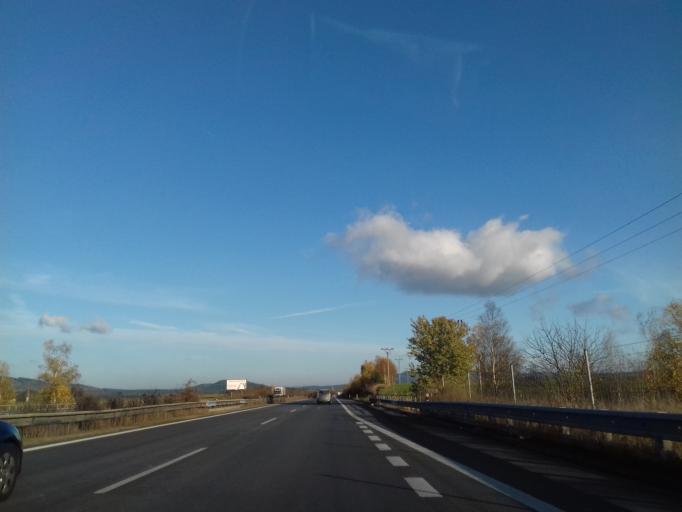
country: CZ
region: Plzensky
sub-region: Okres Rokycany
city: Rokycany
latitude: 49.7547
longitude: 13.5966
